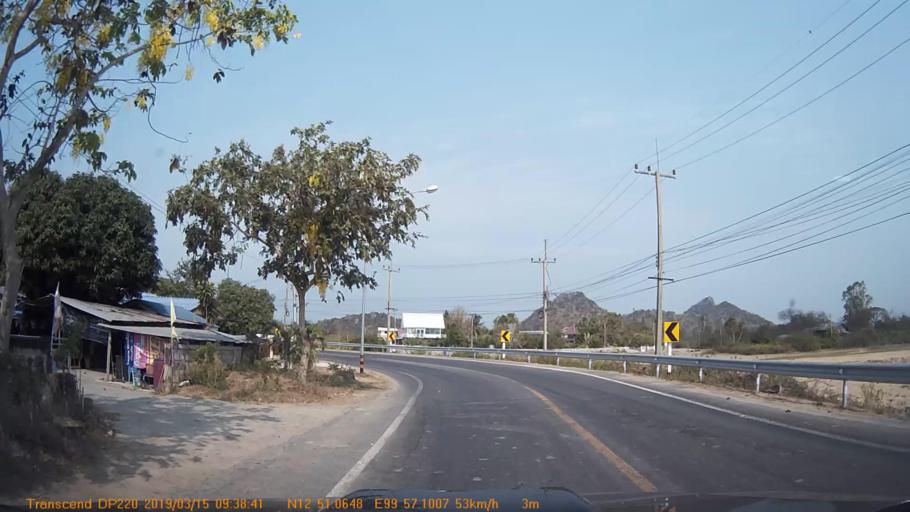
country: TH
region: Phetchaburi
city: Cha-am
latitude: 12.8508
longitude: 99.9510
